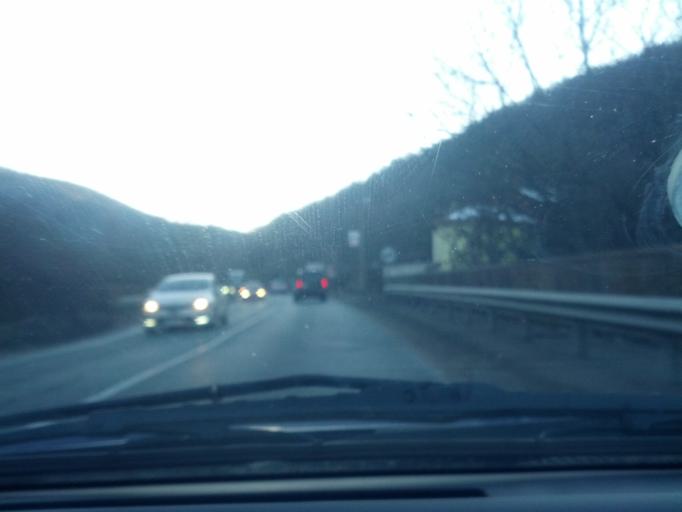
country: BG
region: Vratsa
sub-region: Obshtina Mezdra
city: Mezdra
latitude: 43.0544
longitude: 23.6834
